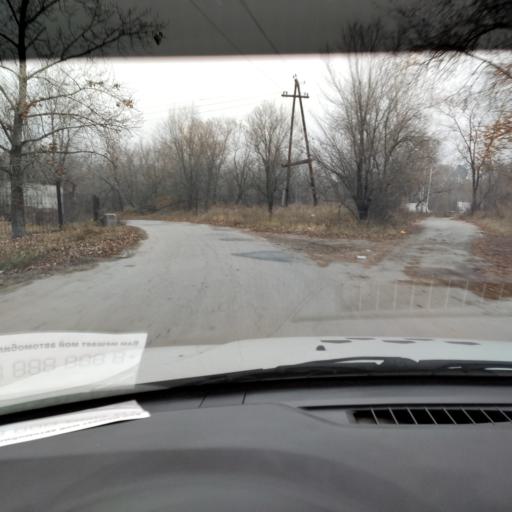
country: RU
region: Samara
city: Zhigulevsk
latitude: 53.4687
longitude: 49.5612
